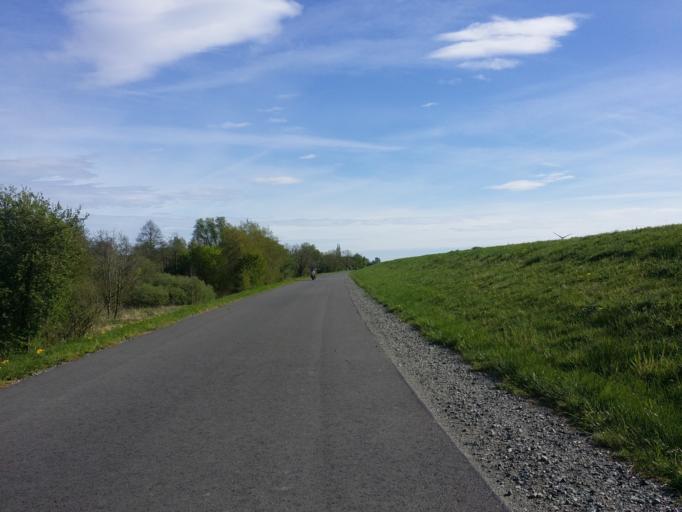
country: DE
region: Lower Saxony
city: Lemwerder
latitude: 53.1418
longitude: 8.6347
